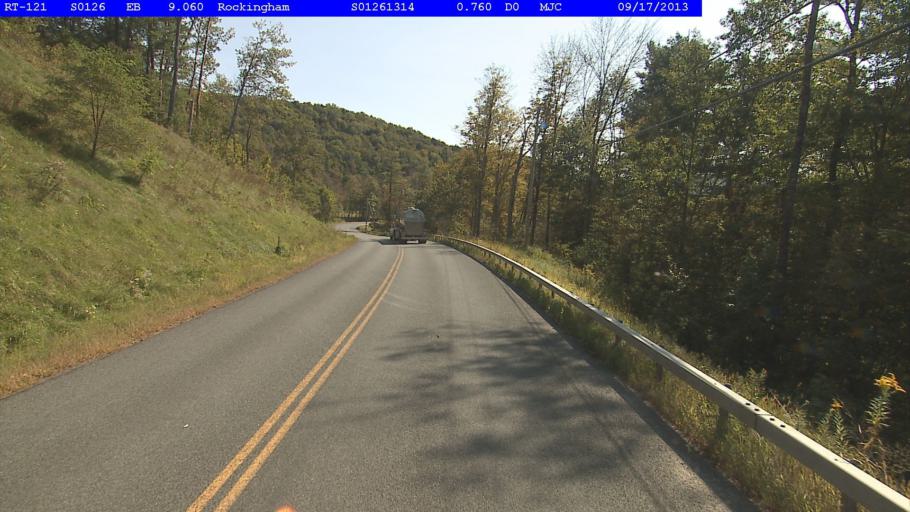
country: US
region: Vermont
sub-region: Windham County
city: Rockingham
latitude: 43.1455
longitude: -72.5455
